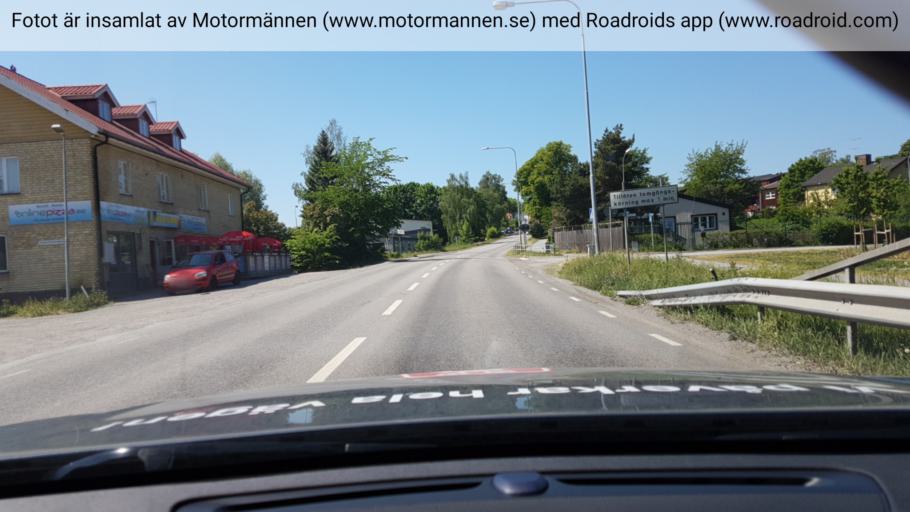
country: SE
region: Stockholm
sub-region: Norrtalje Kommun
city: Rimbo
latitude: 59.7456
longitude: 18.3756
